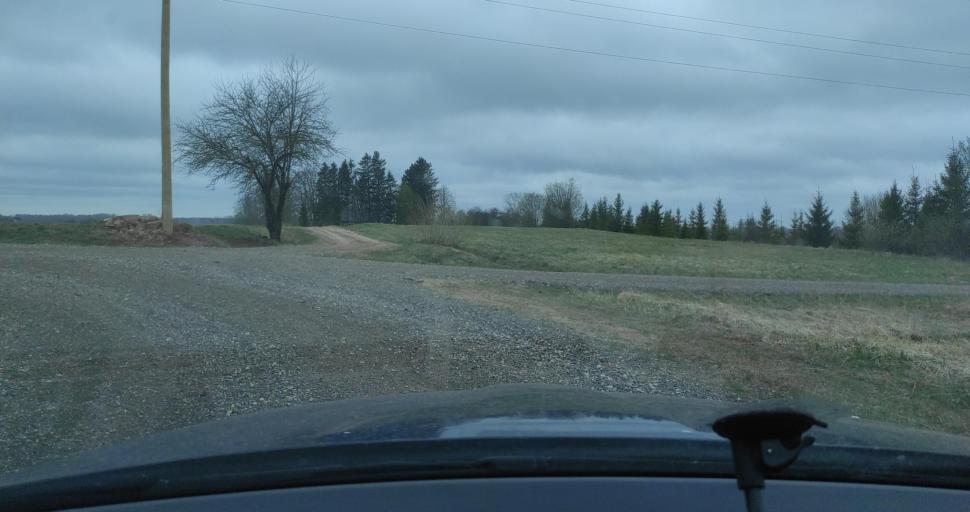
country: LV
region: Saldus Rajons
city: Saldus
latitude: 56.6348
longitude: 22.4244
